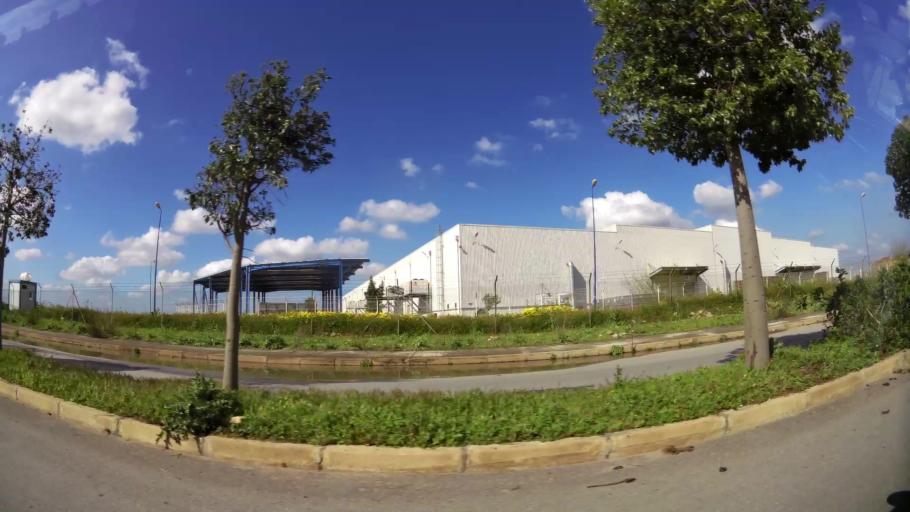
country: MA
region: Grand Casablanca
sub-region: Mediouna
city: Mediouna
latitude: 33.3916
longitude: -7.5460
